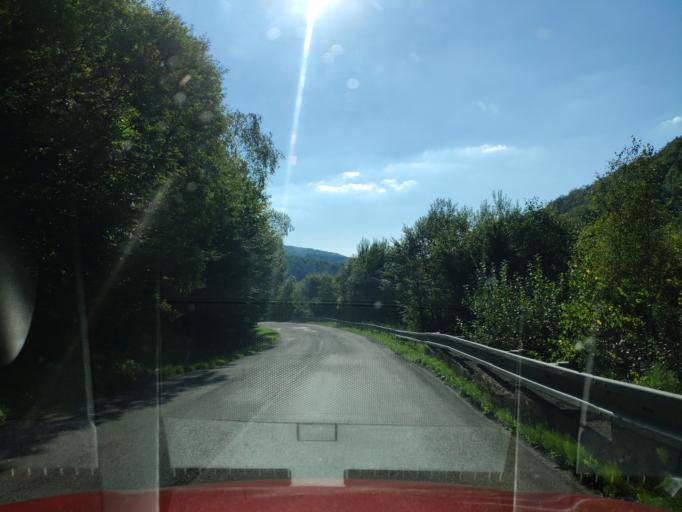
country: SK
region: Presovsky
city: Snina
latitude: 49.0451
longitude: 22.2914
